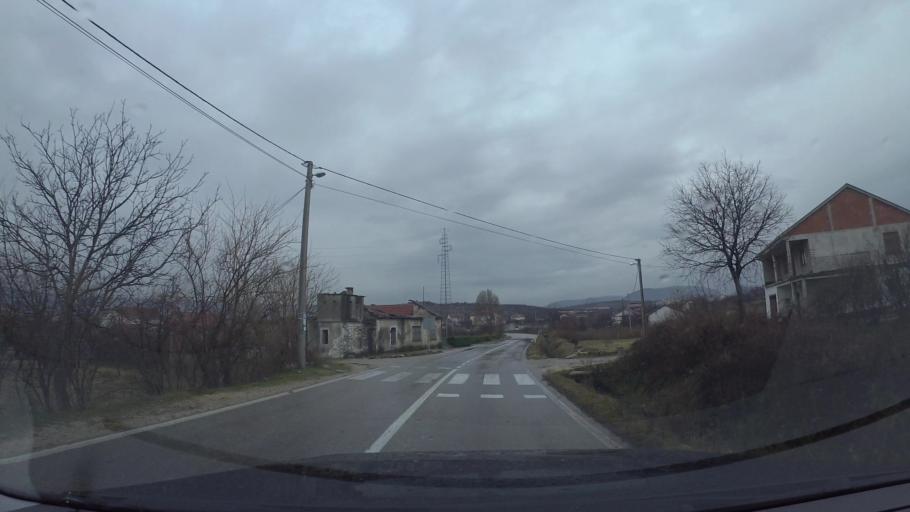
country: BA
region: Federation of Bosnia and Herzegovina
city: Blagaj
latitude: 43.2901
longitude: 17.8574
